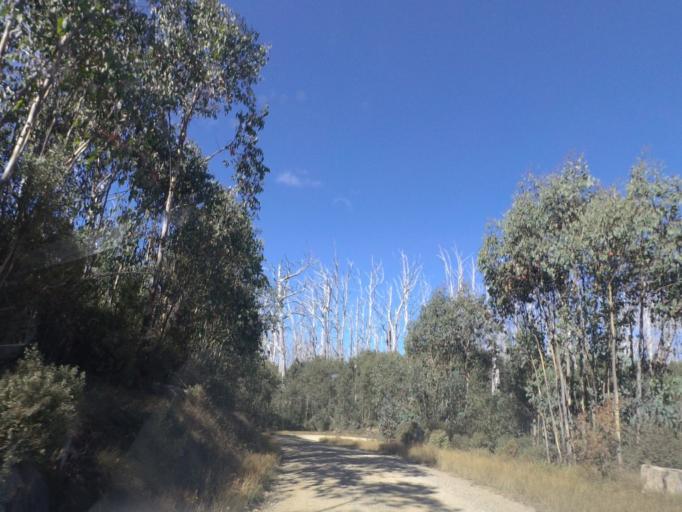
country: AU
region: Victoria
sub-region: Murrindindi
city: Alexandra
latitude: -37.4341
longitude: 145.8041
